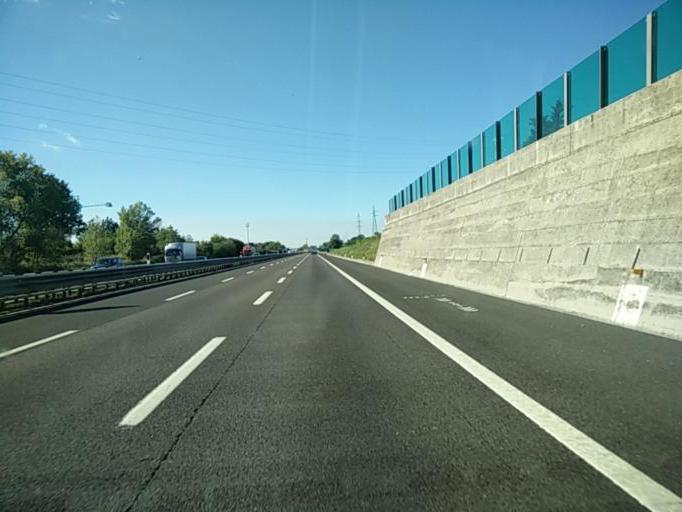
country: IT
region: Veneto
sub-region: Provincia di Verona
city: Cavalcaselle
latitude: 45.4283
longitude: 10.7417
